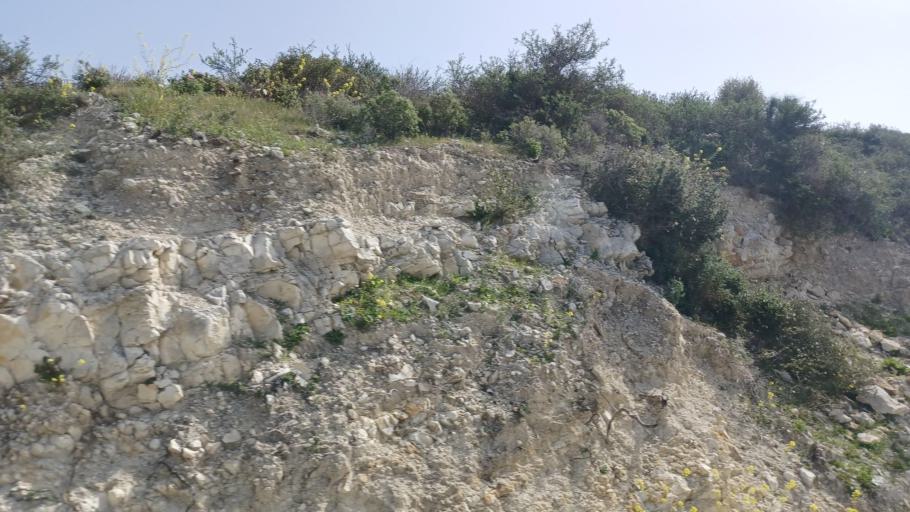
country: CY
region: Limassol
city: Pissouri
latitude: 34.7106
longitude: 32.7086
